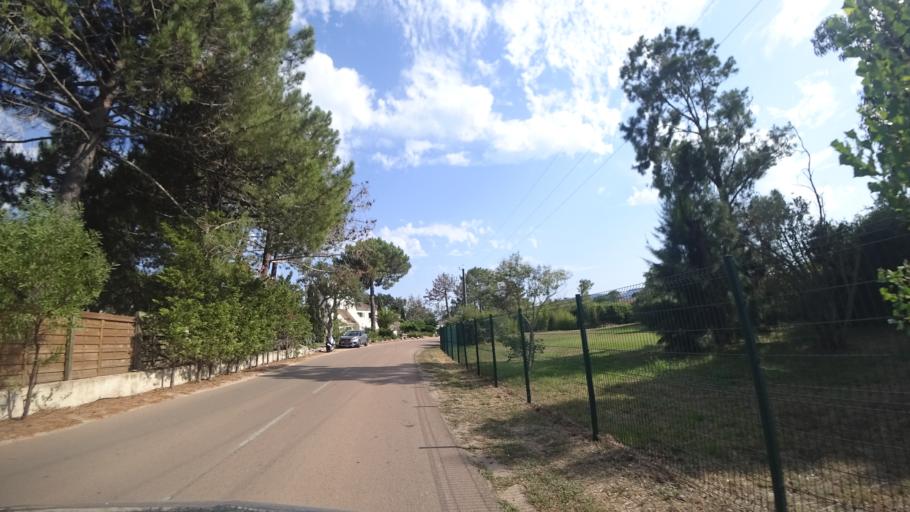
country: FR
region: Corsica
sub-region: Departement de la Corse-du-Sud
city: Porto-Vecchio
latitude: 41.6258
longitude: 9.3368
